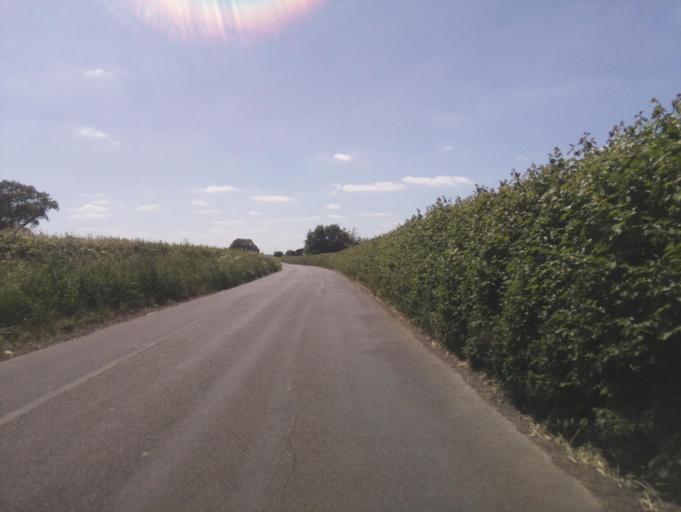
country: GB
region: England
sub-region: Wiltshire
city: Lyneham
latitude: 51.4930
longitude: -1.9269
